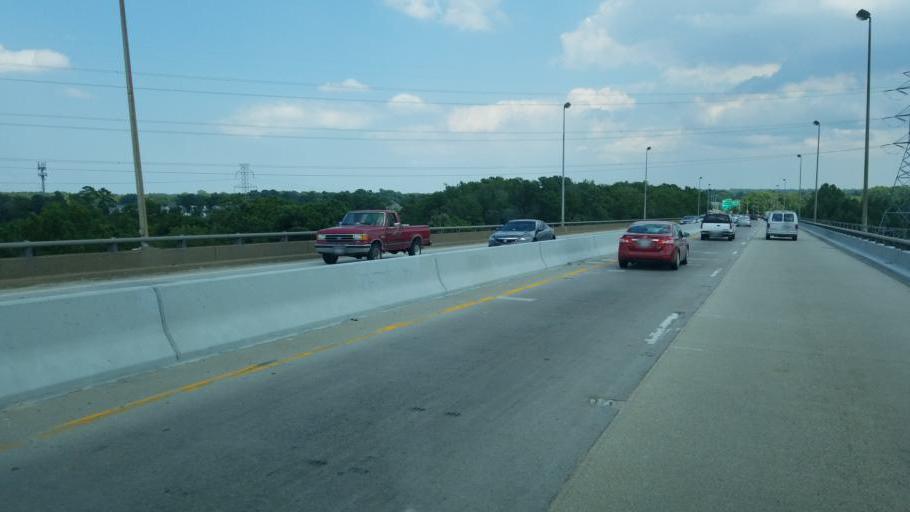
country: US
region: Virginia
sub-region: City of Chesapeake
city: Chesapeake
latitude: 36.7577
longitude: -76.2932
